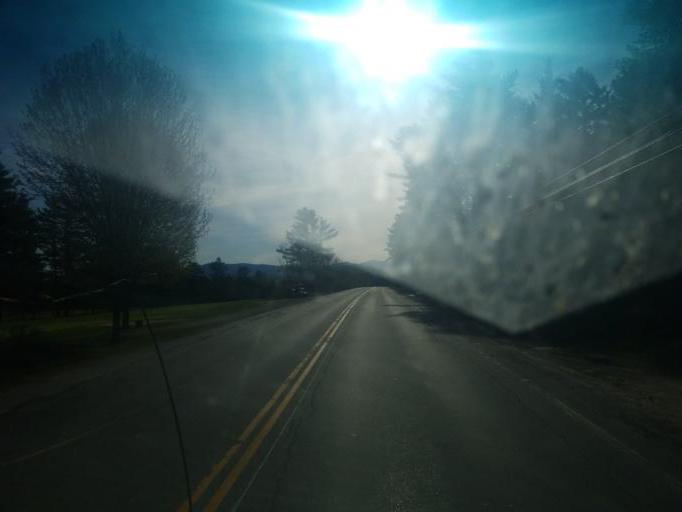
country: US
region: New Hampshire
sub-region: Grafton County
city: Deerfield
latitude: 44.2814
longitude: -71.6707
